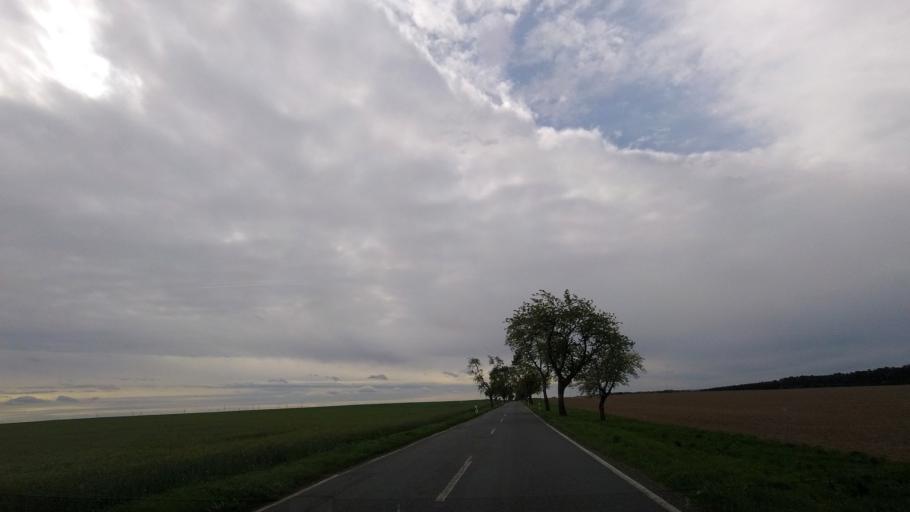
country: DE
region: Brandenburg
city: Dahme
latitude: 51.9138
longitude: 13.4001
